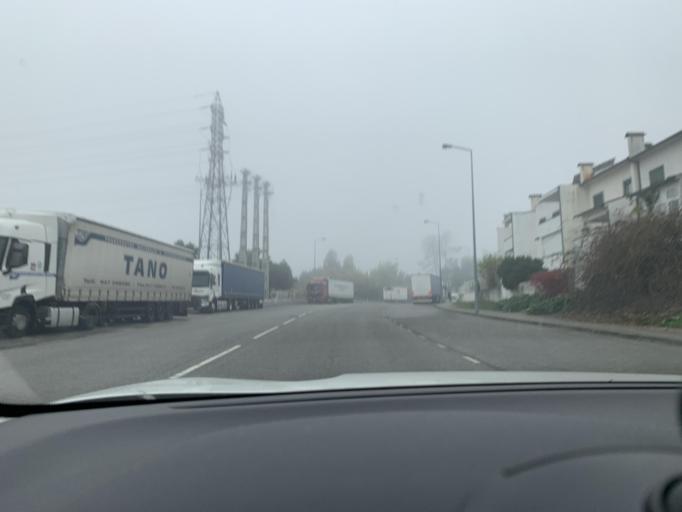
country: PT
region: Viseu
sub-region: Viseu
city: Rio de Loba
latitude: 40.6589
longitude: -7.8808
